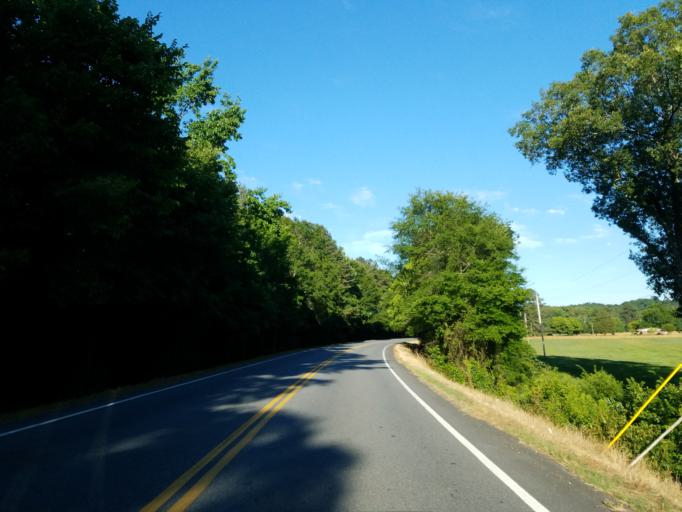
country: US
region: Georgia
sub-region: Gordon County
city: Calhoun
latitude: 34.5411
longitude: -84.9867
